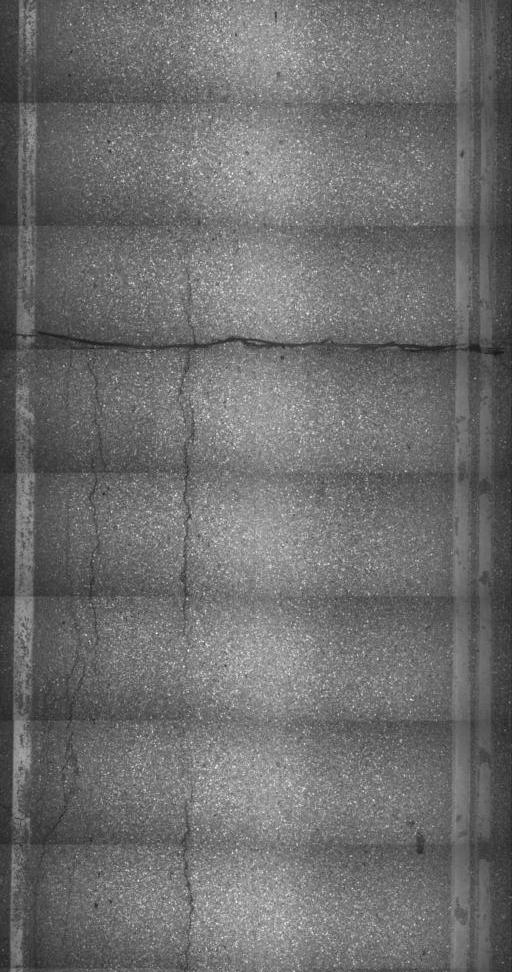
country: US
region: Vermont
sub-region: Franklin County
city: Saint Albans
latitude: 44.7392
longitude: -73.1151
